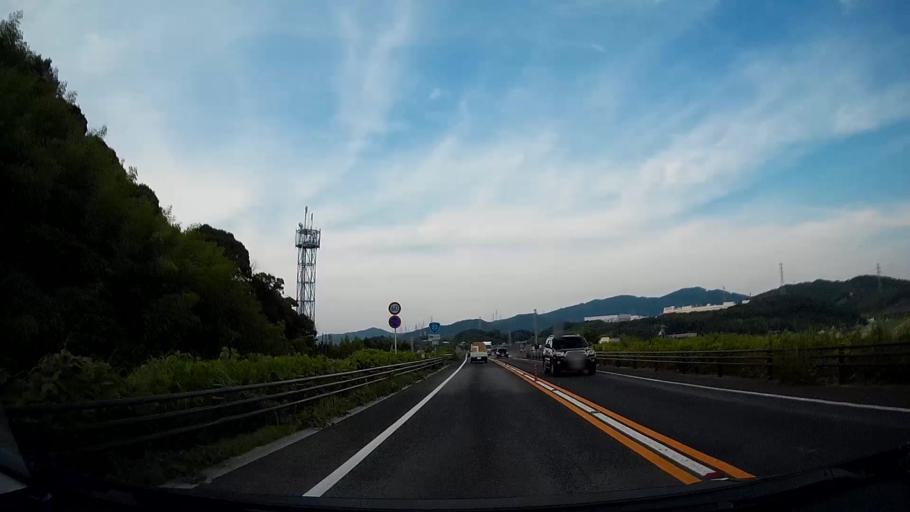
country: JP
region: Aichi
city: Gamagori
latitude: 34.8486
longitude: 137.1611
